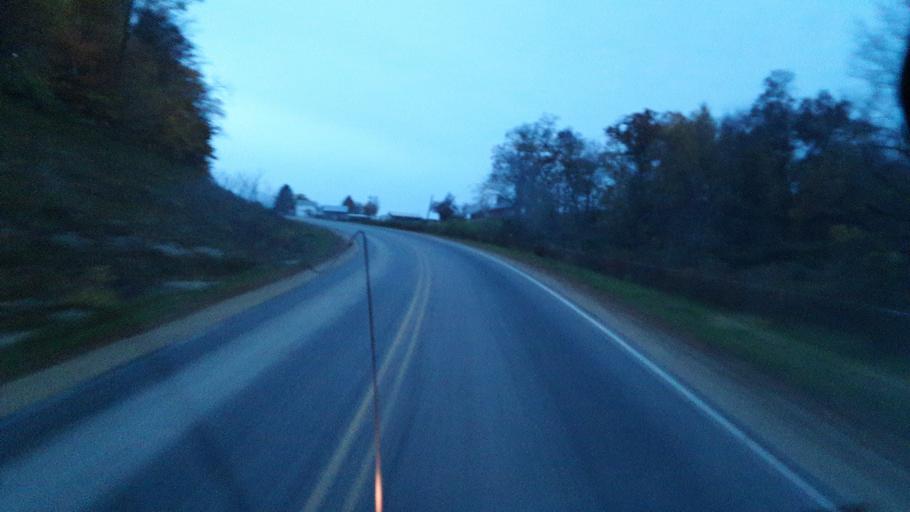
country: US
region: Wisconsin
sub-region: Vernon County
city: Hillsboro
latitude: 43.6463
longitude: -90.4408
